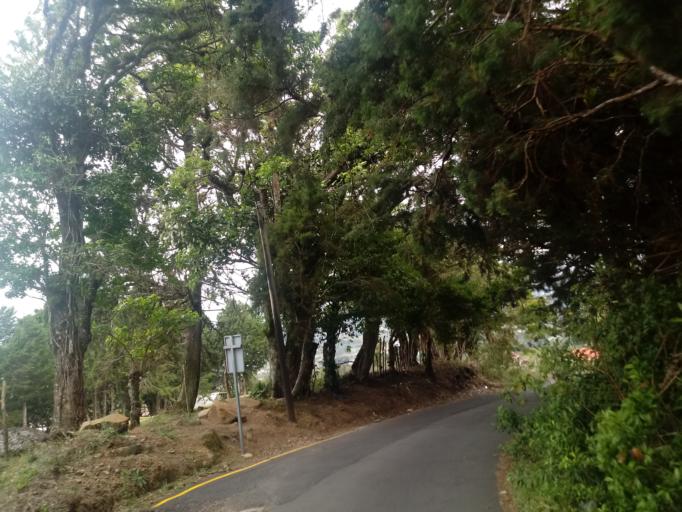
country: CR
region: Heredia
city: Angeles
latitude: 10.0385
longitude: -84.0407
